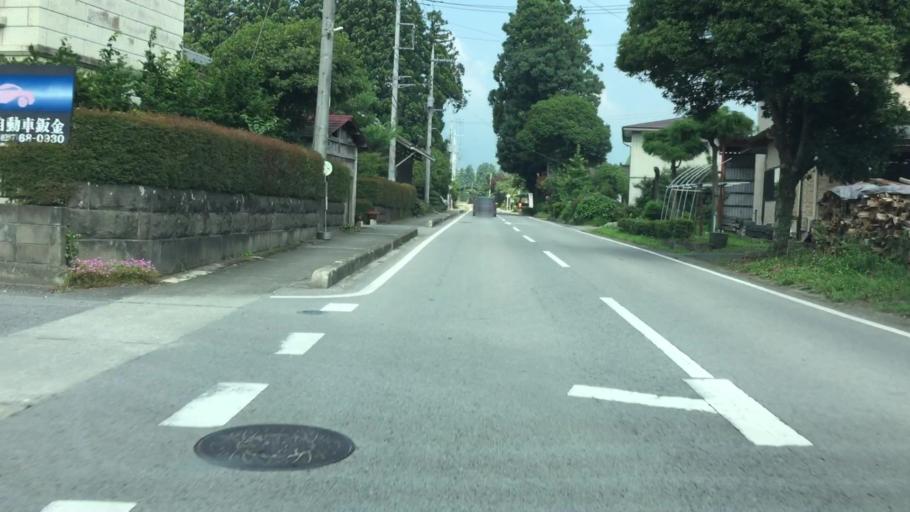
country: JP
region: Tochigi
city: Kuroiso
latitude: 36.9747
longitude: 139.9616
